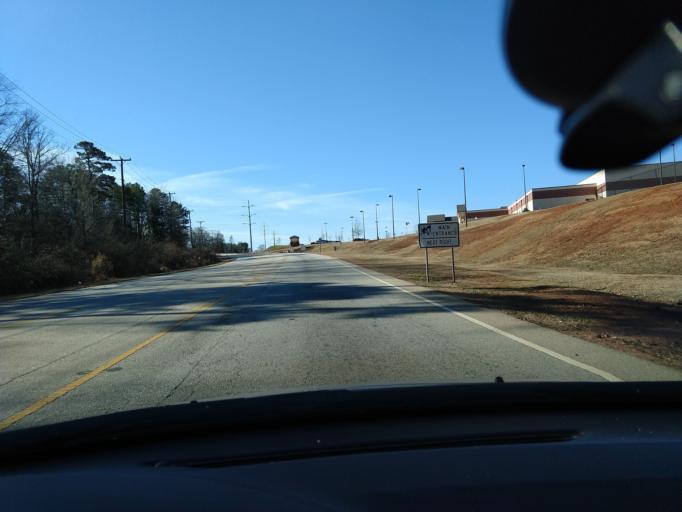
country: US
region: South Carolina
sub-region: Greenville County
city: Mauldin
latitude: 34.8081
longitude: -82.3347
